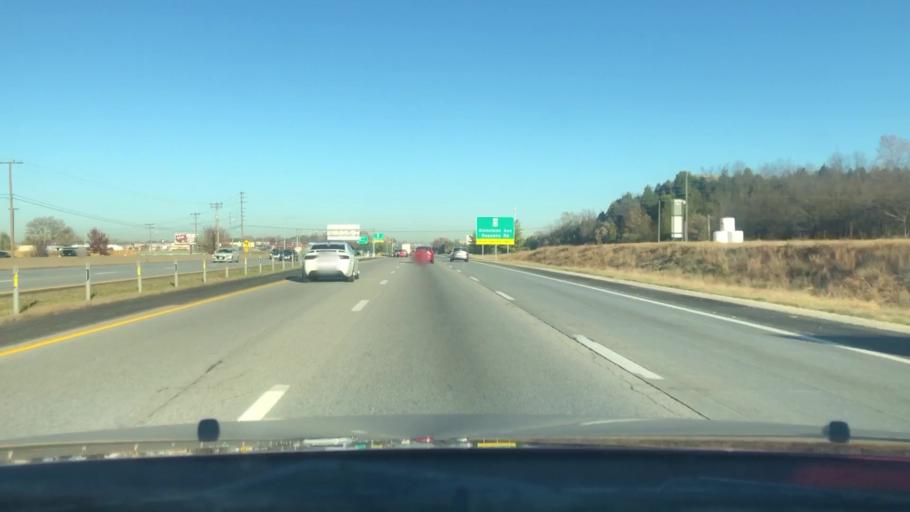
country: US
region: Missouri
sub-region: Greene County
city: Springfield
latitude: 37.1353
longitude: -93.2468
